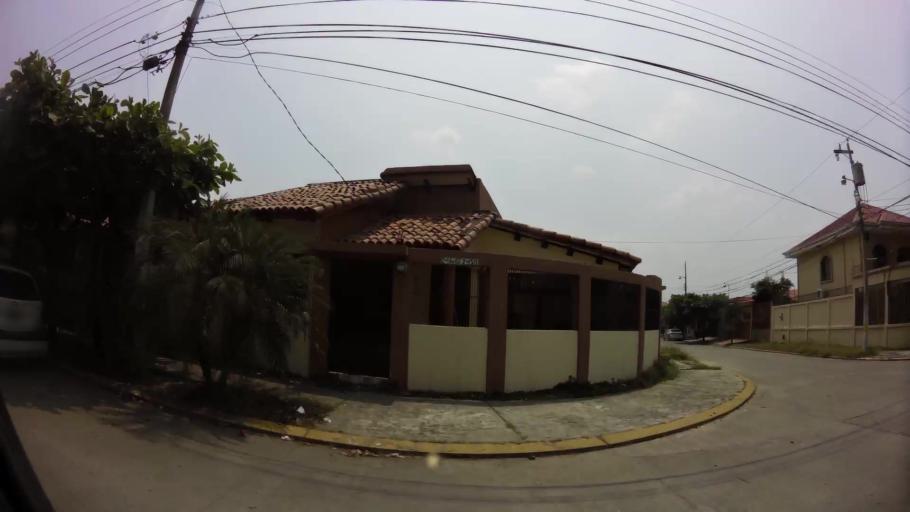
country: HN
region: Cortes
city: San Pedro Sula
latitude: 15.4888
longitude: -88.0006
